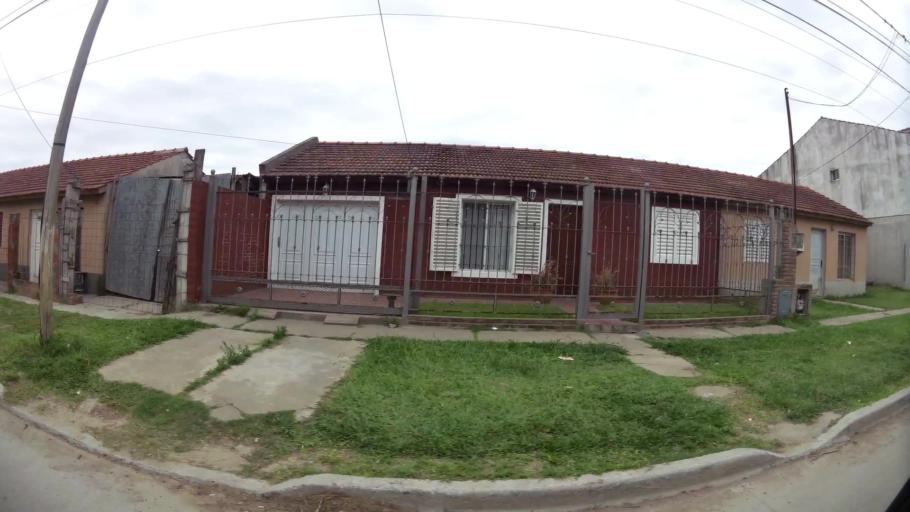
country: AR
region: Buenos Aires
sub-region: Partido de Campana
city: Campana
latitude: -34.2041
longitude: -58.9471
